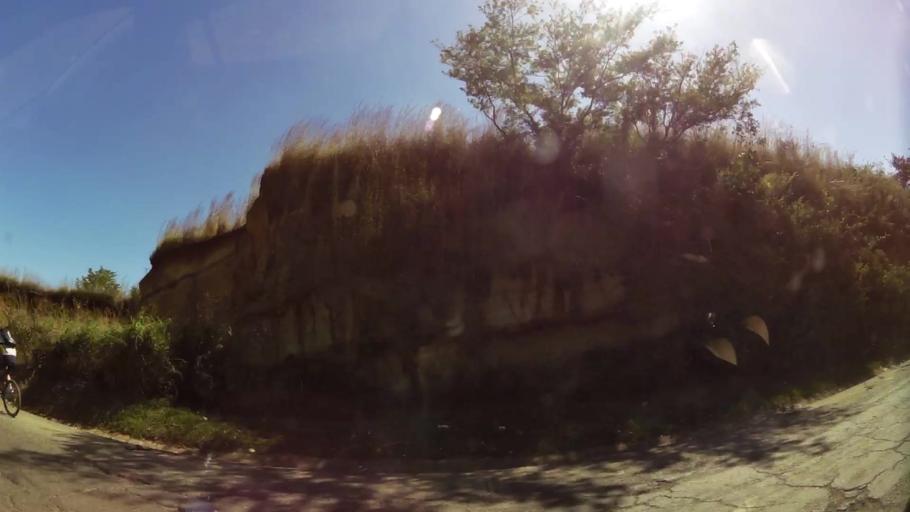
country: SV
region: Ahuachapan
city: Ahuachapan
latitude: 13.9412
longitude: -89.8431
